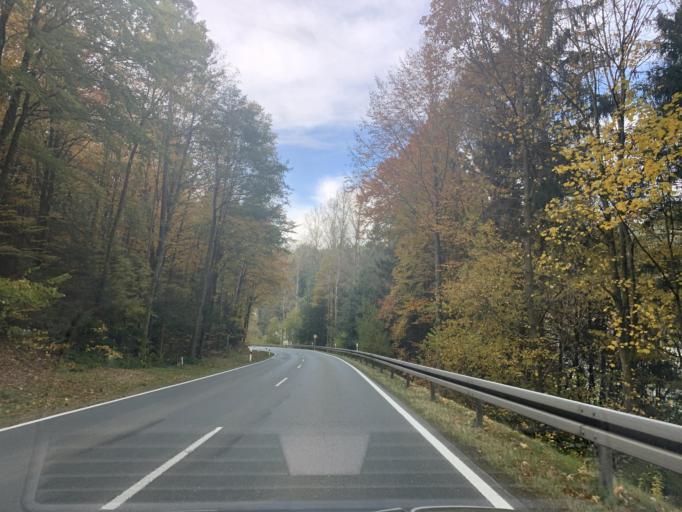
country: DE
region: Bavaria
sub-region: Upper Palatinate
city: Bach
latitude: 49.3834
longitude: 12.3828
